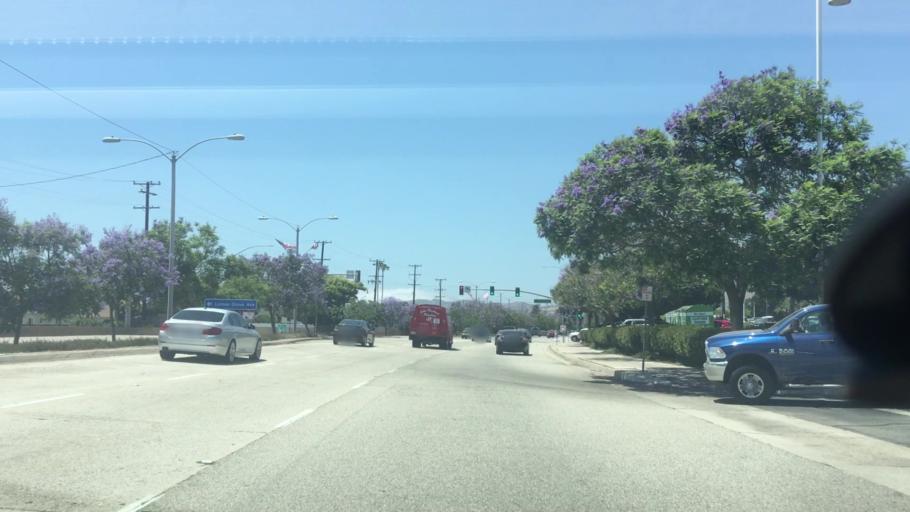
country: US
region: California
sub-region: Ventura County
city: Ventura
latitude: 34.2657
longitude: -119.2479
